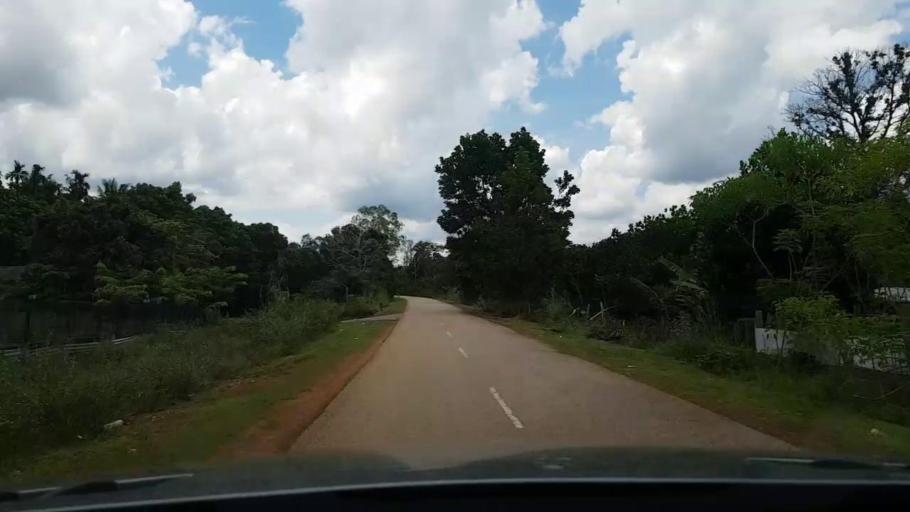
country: MY
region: Pahang
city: Pekan
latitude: 3.1216
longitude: 102.9756
